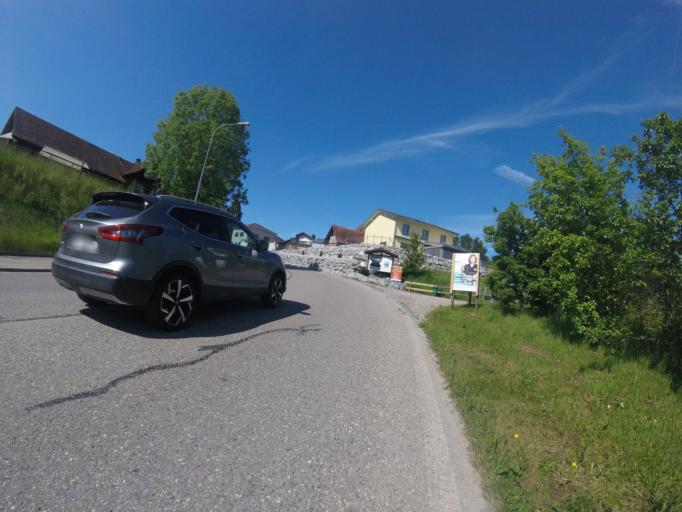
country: CH
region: Saint Gallen
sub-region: Wahlkreis Toggenburg
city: Lutisburg
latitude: 47.4077
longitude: 9.0715
